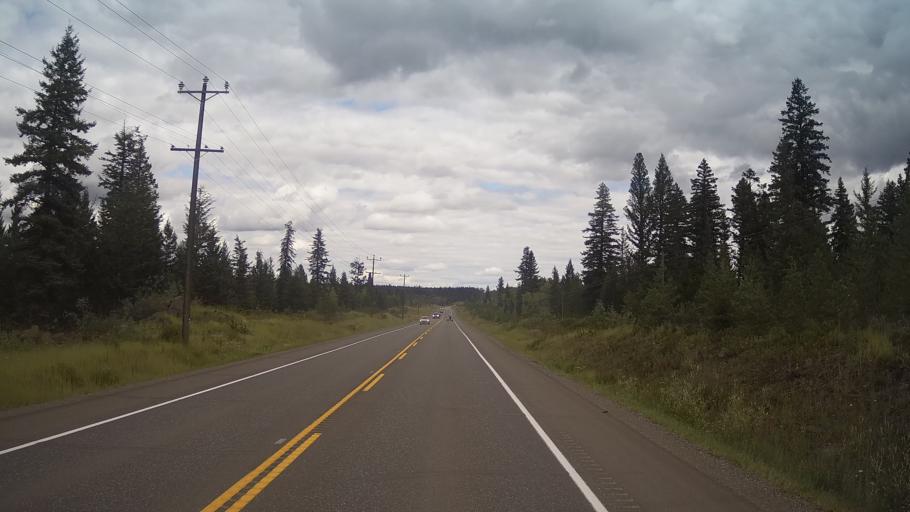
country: CA
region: British Columbia
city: Cache Creek
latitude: 51.2493
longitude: -121.4794
